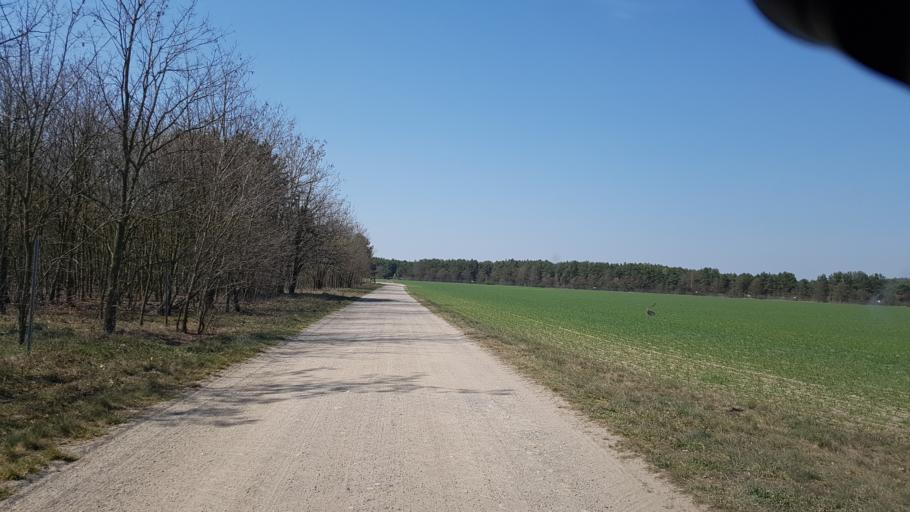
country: DE
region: Saxony-Anhalt
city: Holzdorf
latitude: 51.7587
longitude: 13.1896
